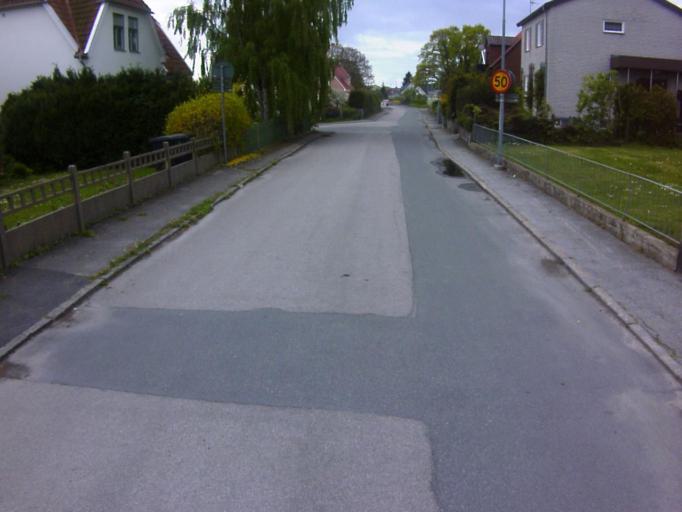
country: SE
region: Blekinge
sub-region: Solvesborgs Kommun
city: Soelvesborg
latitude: 56.0491
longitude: 14.5752
